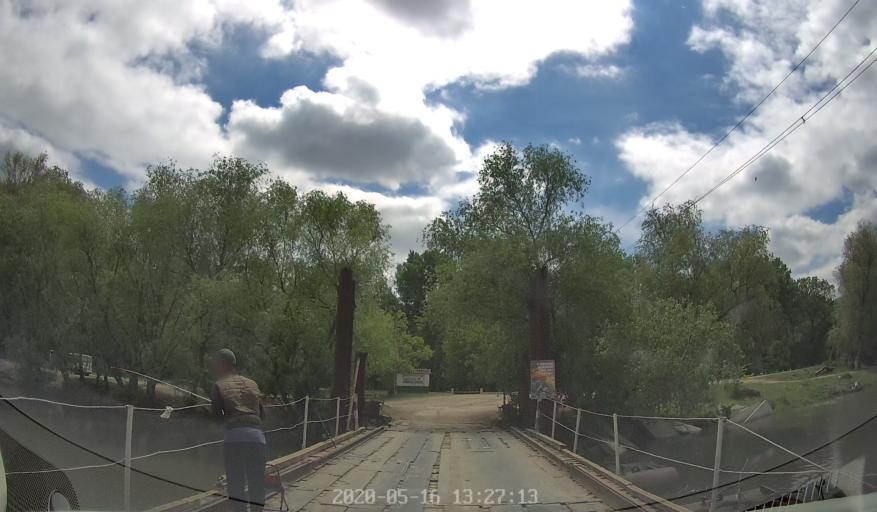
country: MD
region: Telenesti
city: Dnestrovsc
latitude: 46.5464
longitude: 30.0000
